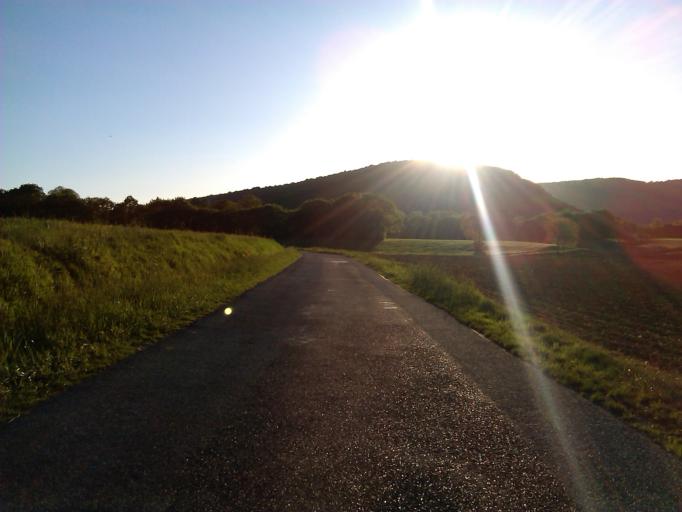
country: FR
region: Franche-Comte
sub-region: Departement du Doubs
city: Clerval
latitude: 47.3609
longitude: 6.4477
